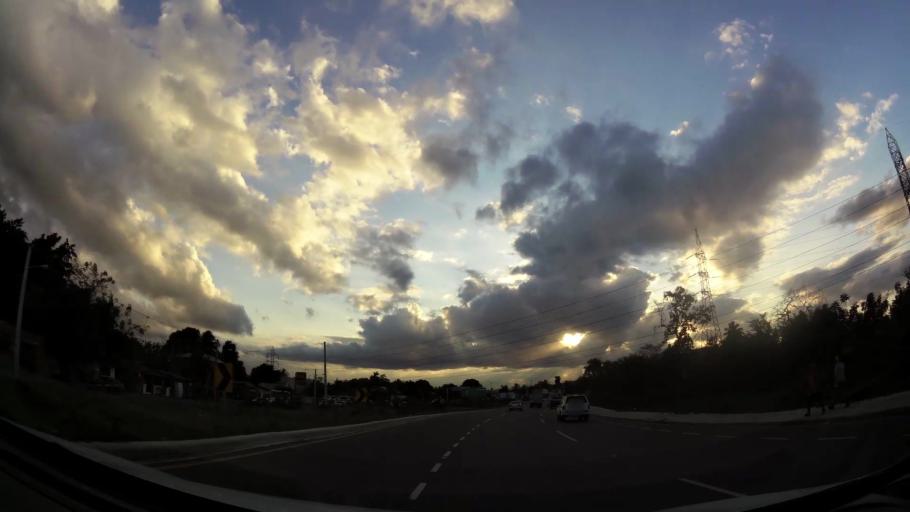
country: DO
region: Santiago
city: Licey al Medio
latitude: 19.4132
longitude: -70.6453
